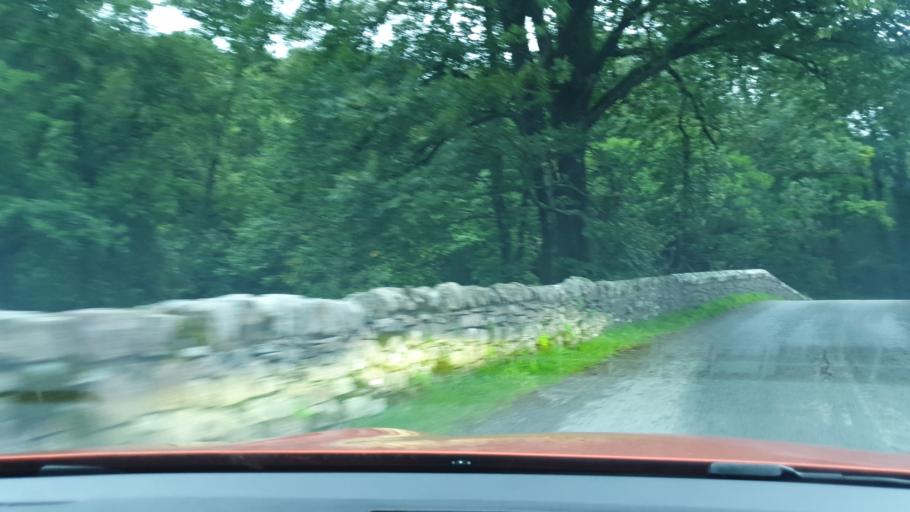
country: GB
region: England
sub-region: Cumbria
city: Seascale
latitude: 54.3844
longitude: -3.3115
